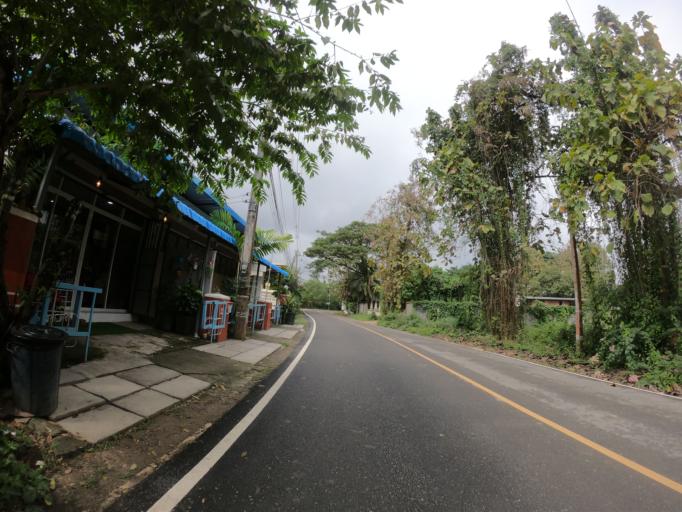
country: TH
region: Chiang Mai
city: San Sai
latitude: 18.8451
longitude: 99.0028
